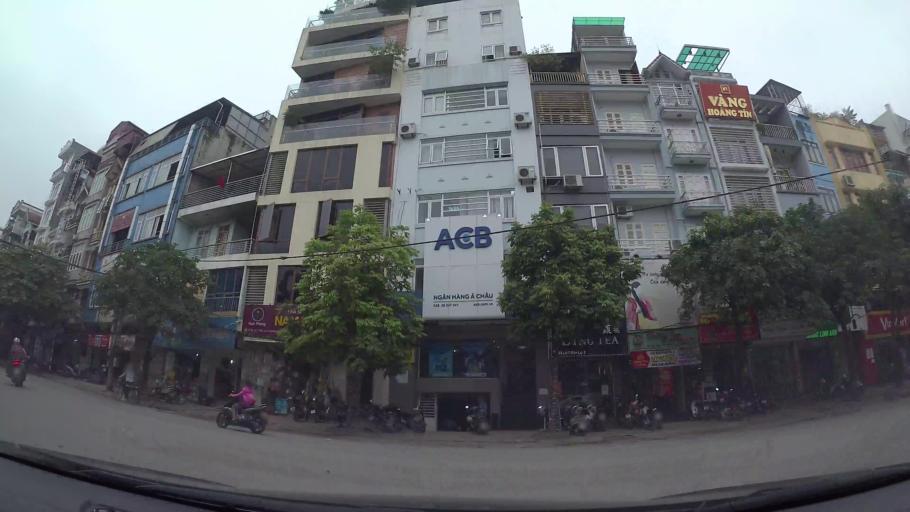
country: VN
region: Ha Noi
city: Hai BaTrung
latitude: 20.9858
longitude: 105.8578
